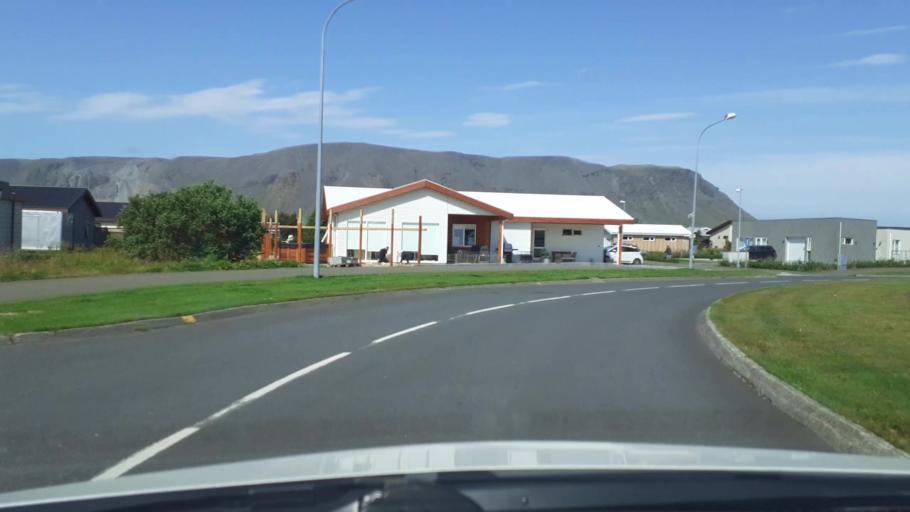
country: IS
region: South
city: Selfoss
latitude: 63.9339
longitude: -21.0205
